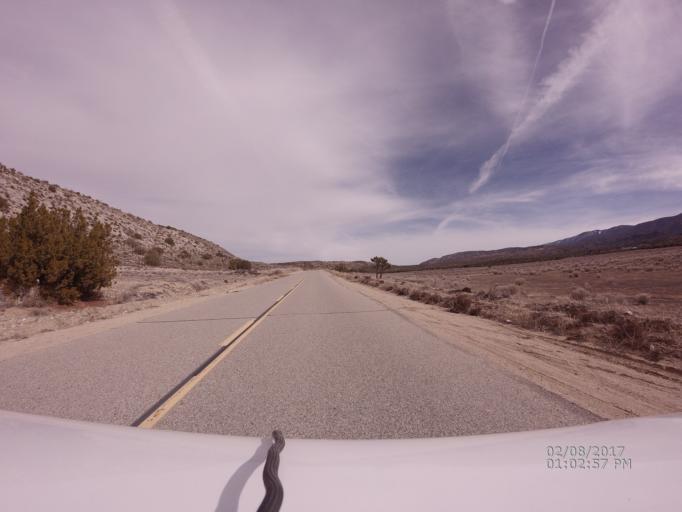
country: US
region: California
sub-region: Los Angeles County
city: Lake Los Angeles
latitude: 34.4501
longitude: -117.8196
